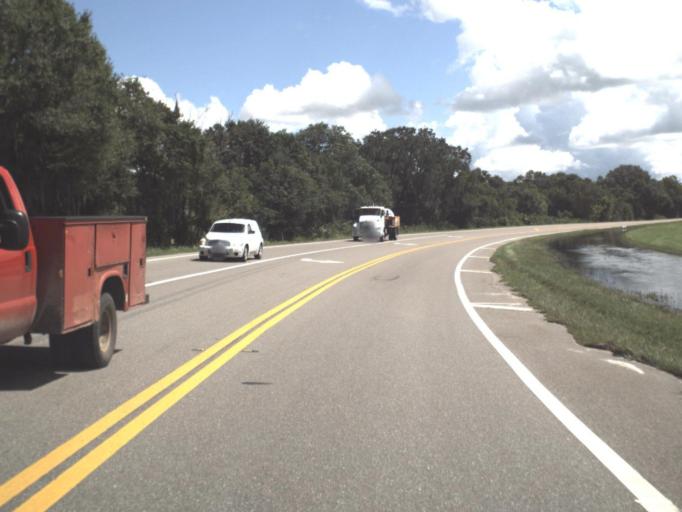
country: US
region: Florida
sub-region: Sarasota County
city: Lake Sarasota
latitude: 27.3871
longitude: -82.2501
